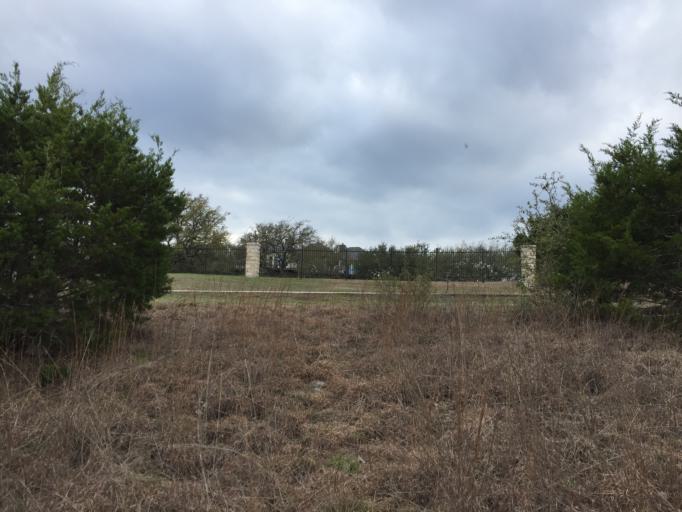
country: US
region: Texas
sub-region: Travis County
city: Shady Hollow
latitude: 30.1461
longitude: -97.9709
